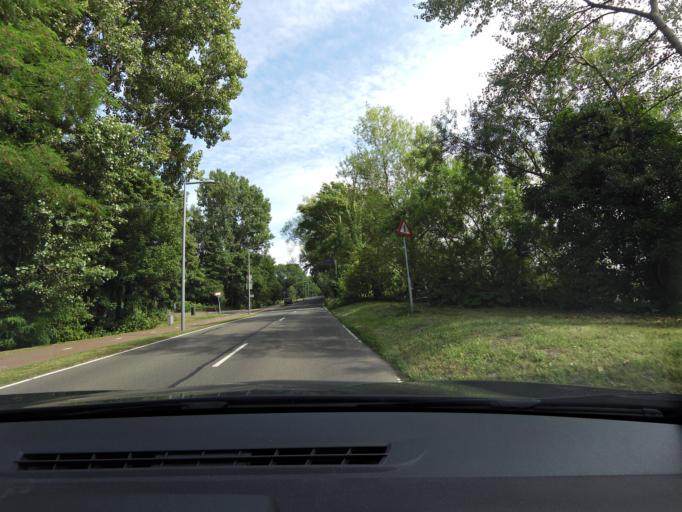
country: NL
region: South Holland
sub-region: Gemeente Schiedam
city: Schiedam
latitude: 51.9555
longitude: 4.4014
